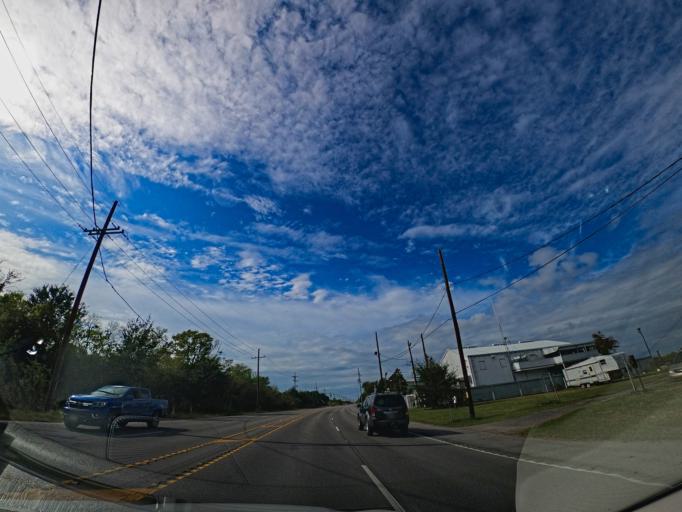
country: US
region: Louisiana
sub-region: Saint Tammany Parish
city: Eden Isle
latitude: 30.0687
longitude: -89.8358
